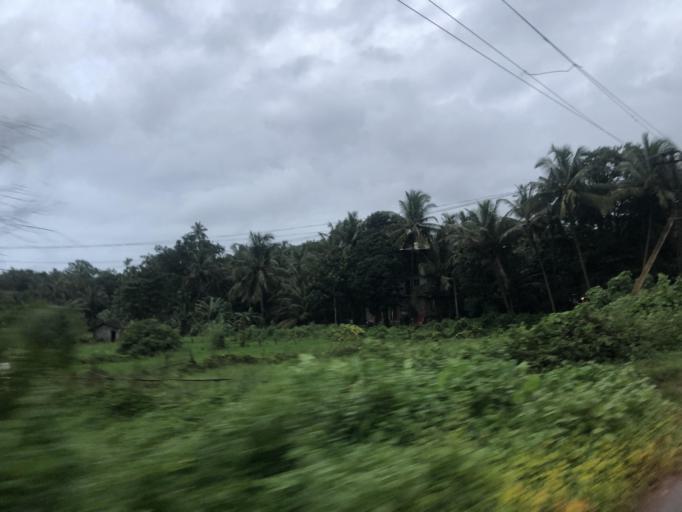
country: IN
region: Goa
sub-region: North Goa
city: Serula
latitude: 15.5520
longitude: 73.8211
